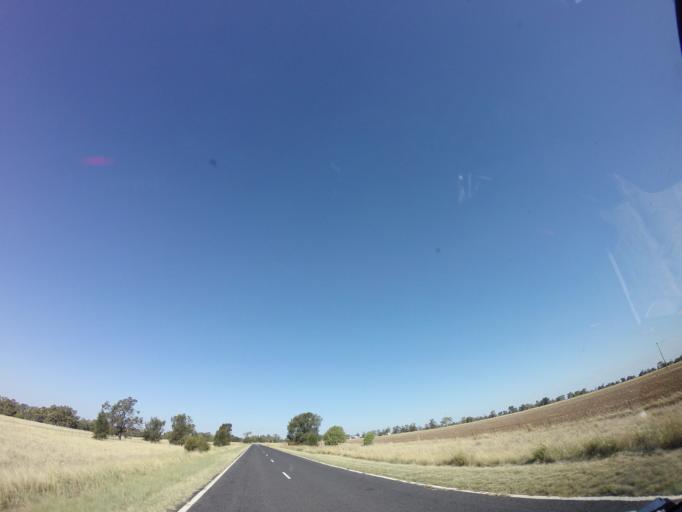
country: AU
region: New South Wales
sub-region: Gilgandra
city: Gilgandra
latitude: -31.6628
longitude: 148.3970
